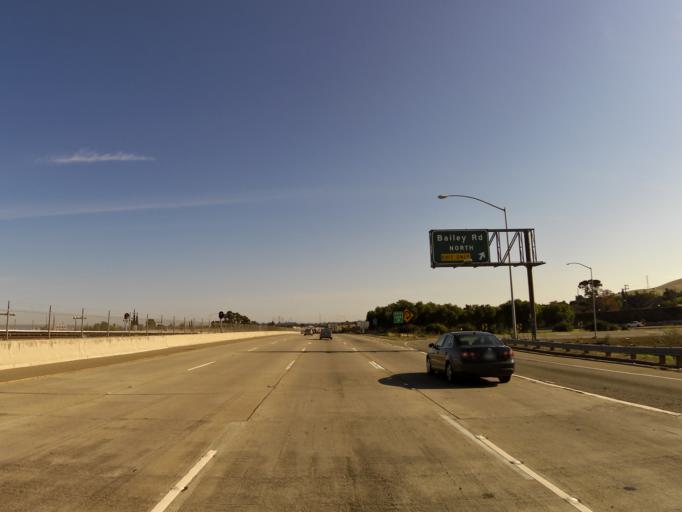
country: US
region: California
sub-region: Contra Costa County
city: Bay Point
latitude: 38.0187
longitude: -121.9418
